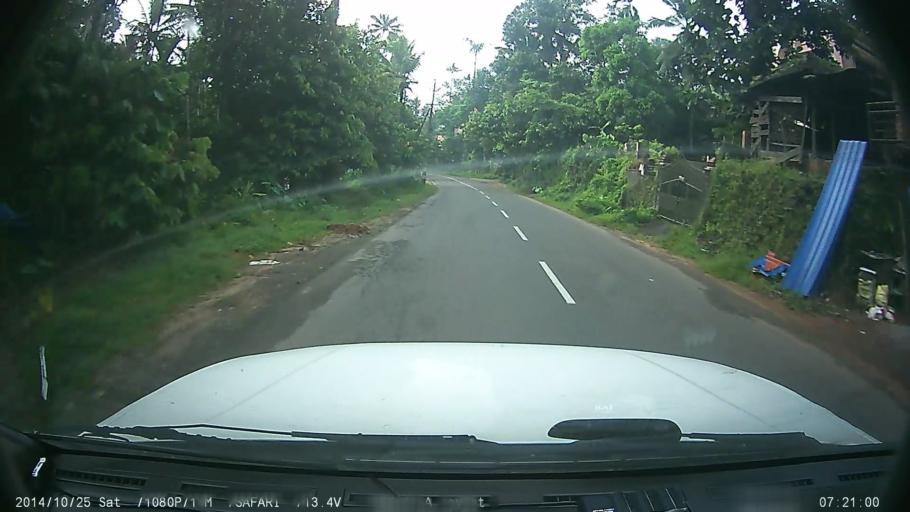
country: IN
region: Kerala
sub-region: Kottayam
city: Palackattumala
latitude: 9.8030
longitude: 76.5749
